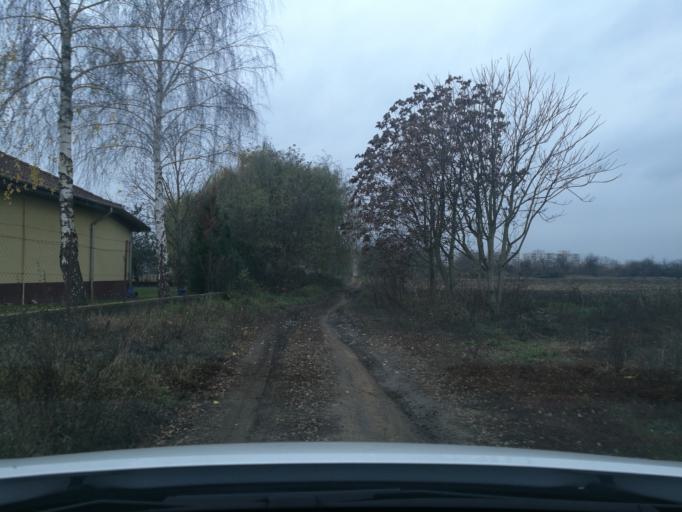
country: HU
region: Szabolcs-Szatmar-Bereg
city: Nyiregyhaza
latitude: 47.9570
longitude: 21.7508
